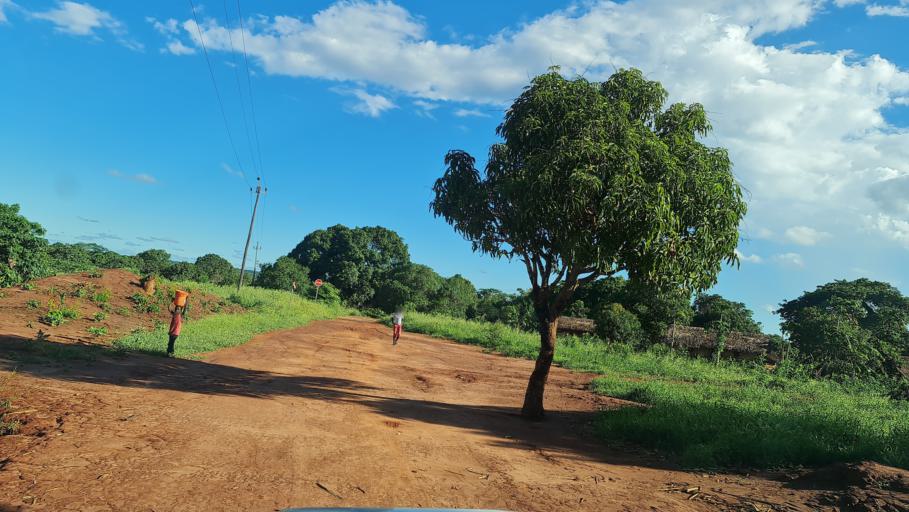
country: MZ
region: Nampula
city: Ilha de Mocambique
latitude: -14.9227
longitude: 40.2185
